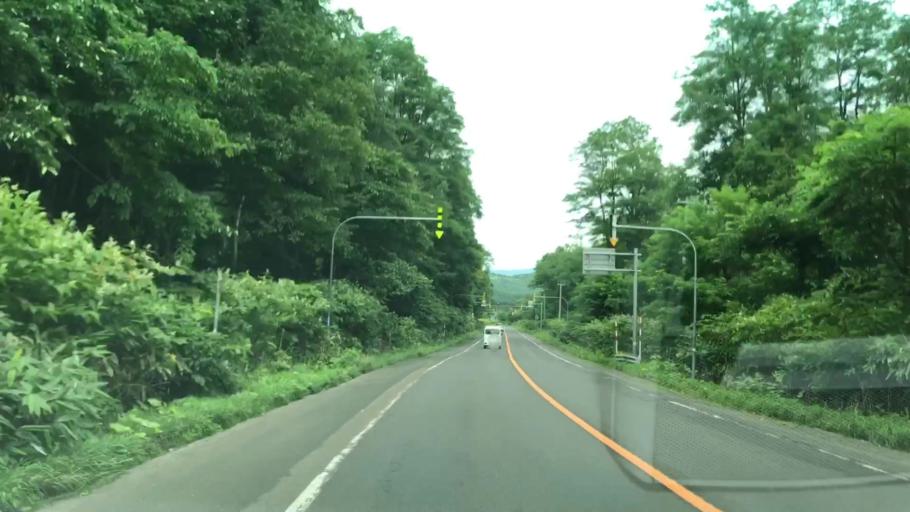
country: JP
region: Hokkaido
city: Niseko Town
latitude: 42.9529
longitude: 140.6974
